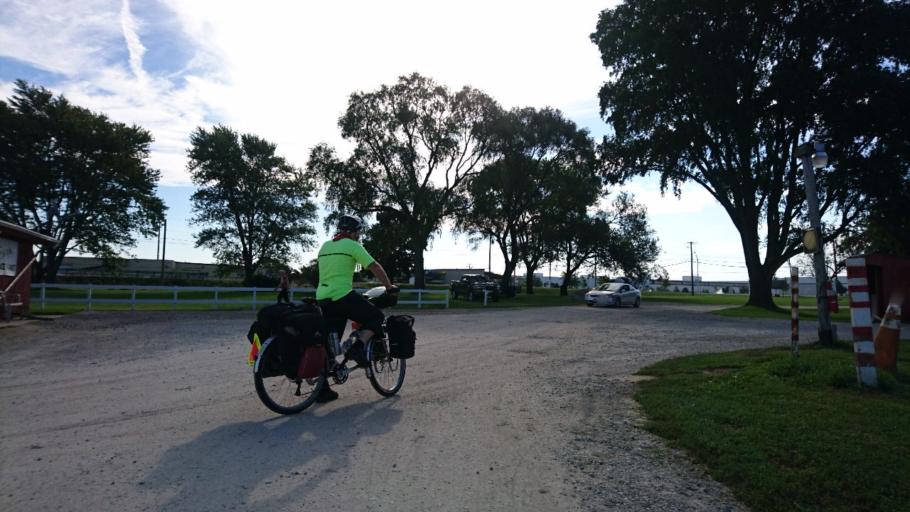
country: US
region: Illinois
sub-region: Will County
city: Ingalls Park
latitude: 41.5118
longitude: -88.0247
